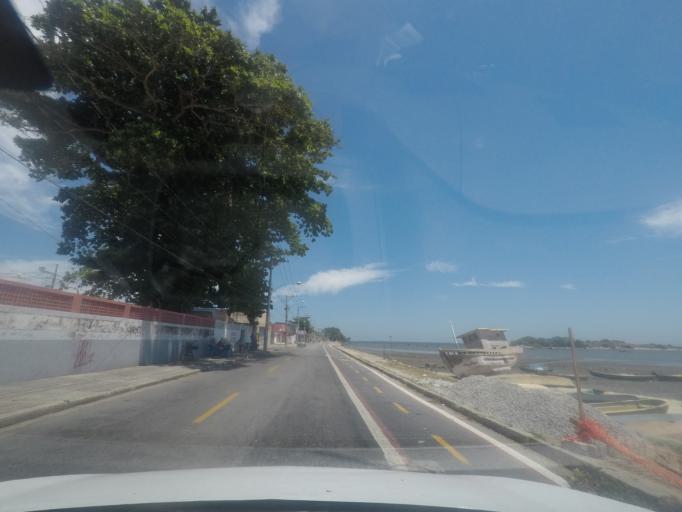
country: BR
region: Rio de Janeiro
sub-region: Itaguai
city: Itaguai
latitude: -22.9800
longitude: -43.7032
